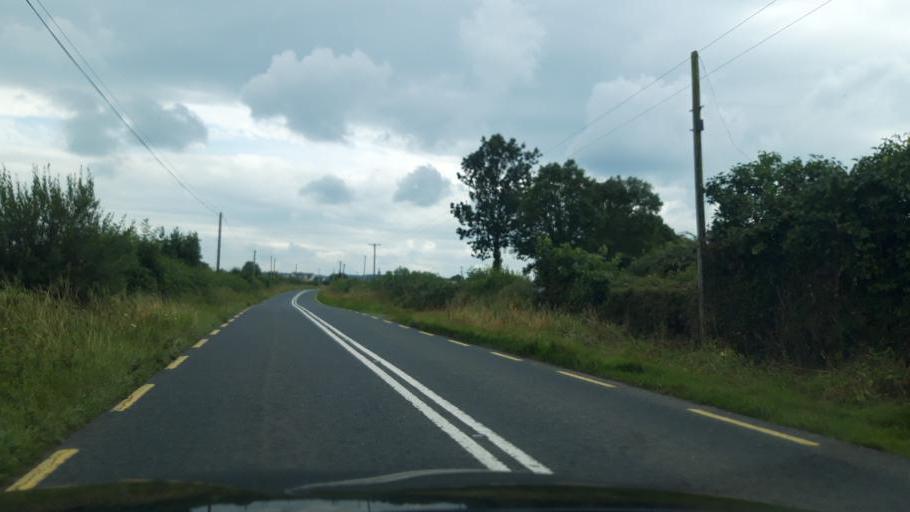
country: IE
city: Ballylinan
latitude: 52.9262
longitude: -7.0615
